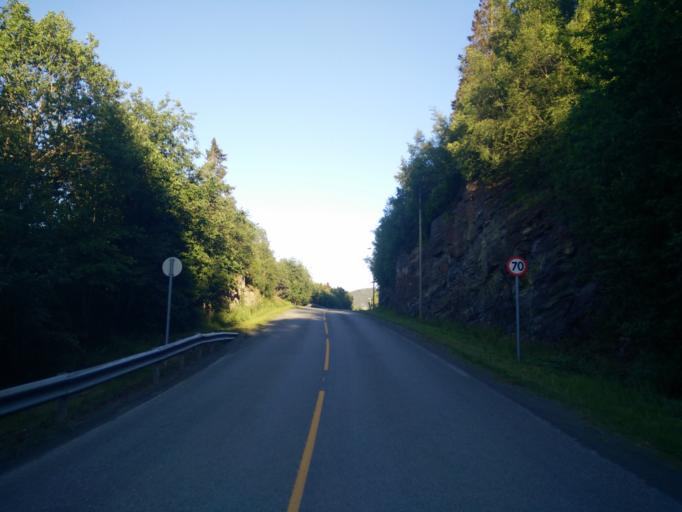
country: NO
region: Sor-Trondelag
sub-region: Skaun
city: Borsa
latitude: 63.3440
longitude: 10.0508
